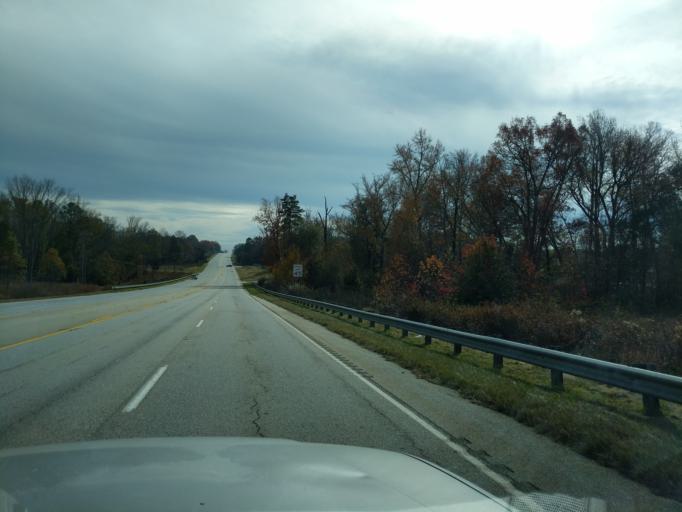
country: US
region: South Carolina
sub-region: Spartanburg County
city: Roebuck
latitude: 34.8515
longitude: -82.0125
